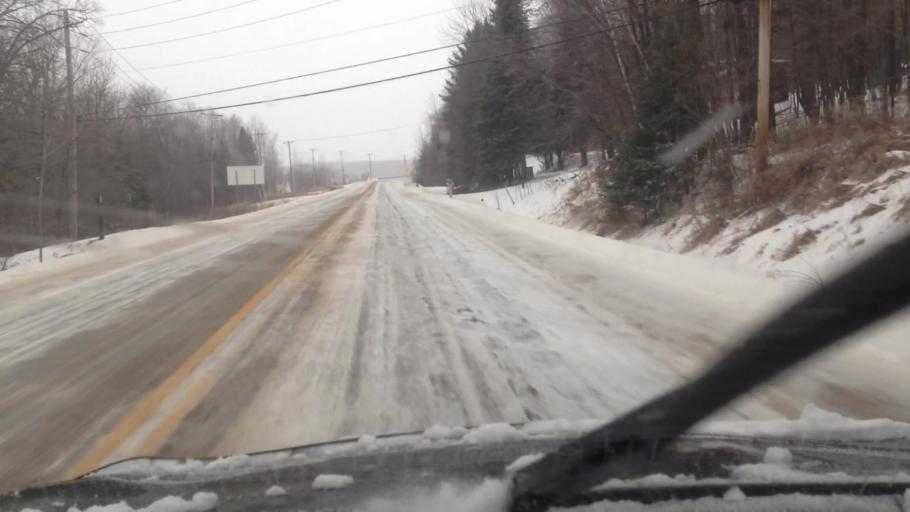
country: CA
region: Quebec
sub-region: Laurentides
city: Mont-Tremblant
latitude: 45.9477
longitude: -74.5602
